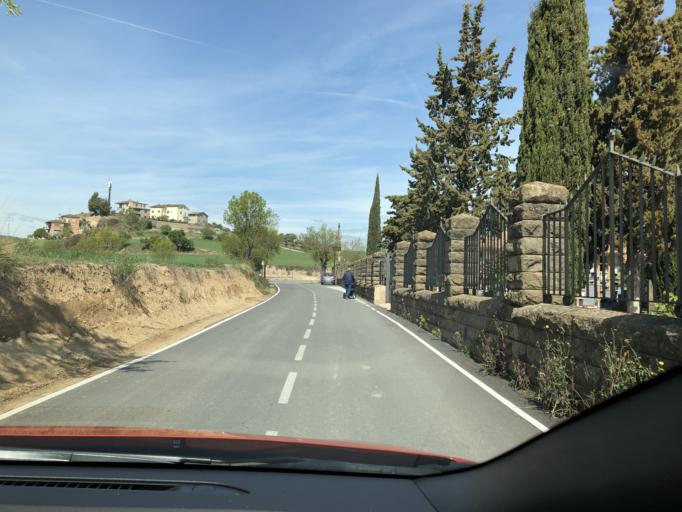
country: ES
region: Catalonia
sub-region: Provincia de Lleida
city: Solsona
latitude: 41.9988
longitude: 1.5250
